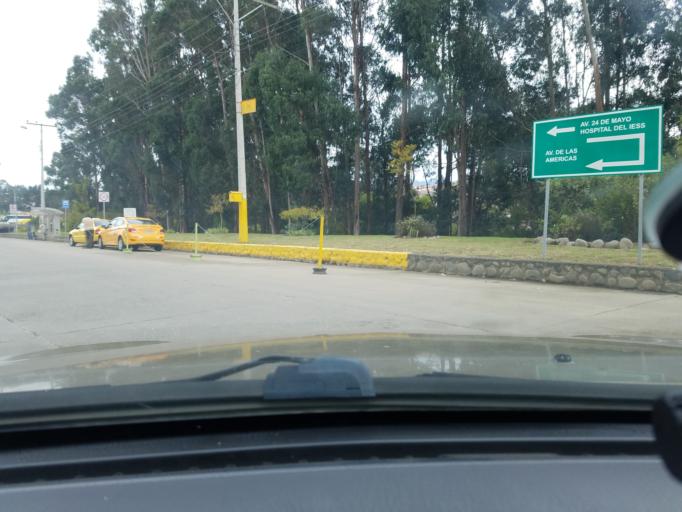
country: EC
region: Azuay
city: Cuenca
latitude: -2.8924
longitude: -78.9606
